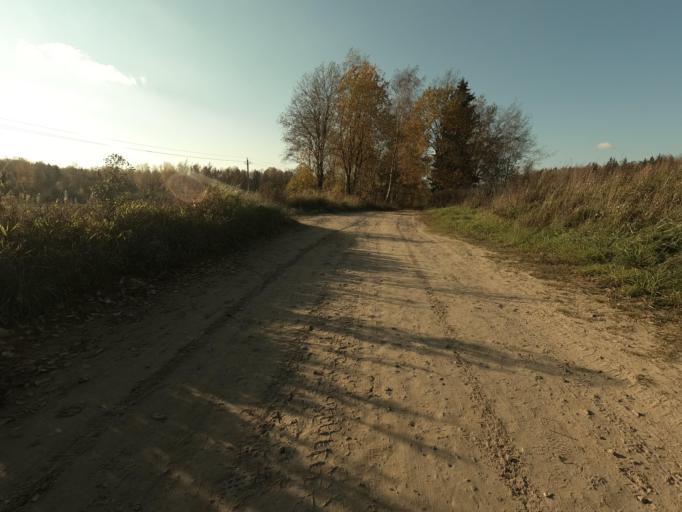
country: RU
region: Leningrad
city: Luppolovo
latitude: 60.1458
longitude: 30.2420
